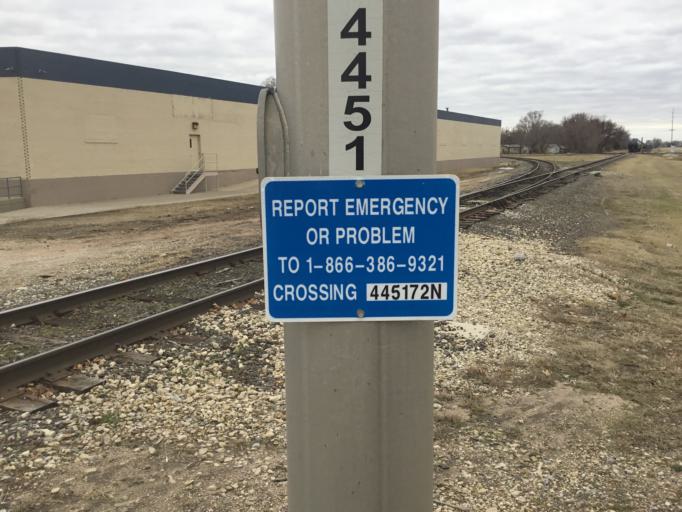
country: US
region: Kansas
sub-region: Sedgwick County
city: Wichita
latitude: 37.6658
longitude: -97.3782
